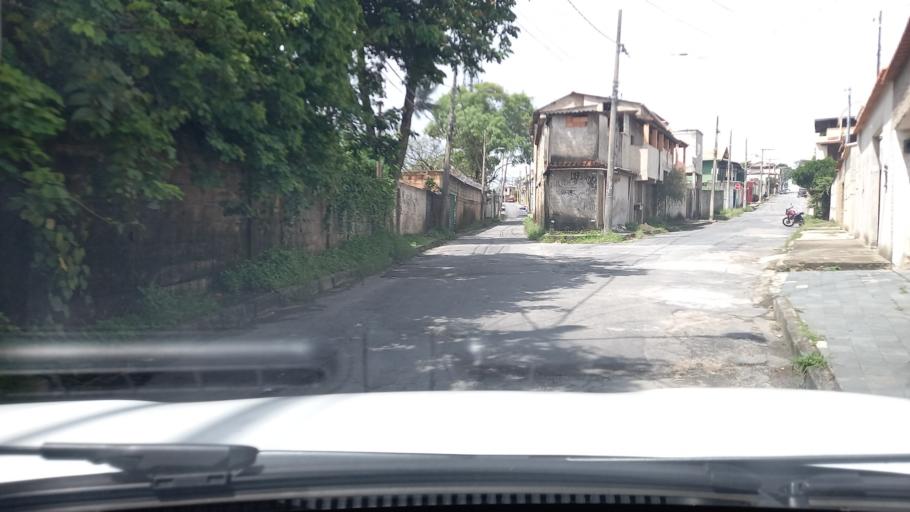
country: BR
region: Minas Gerais
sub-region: Contagem
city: Contagem
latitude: -19.8982
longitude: -44.0232
